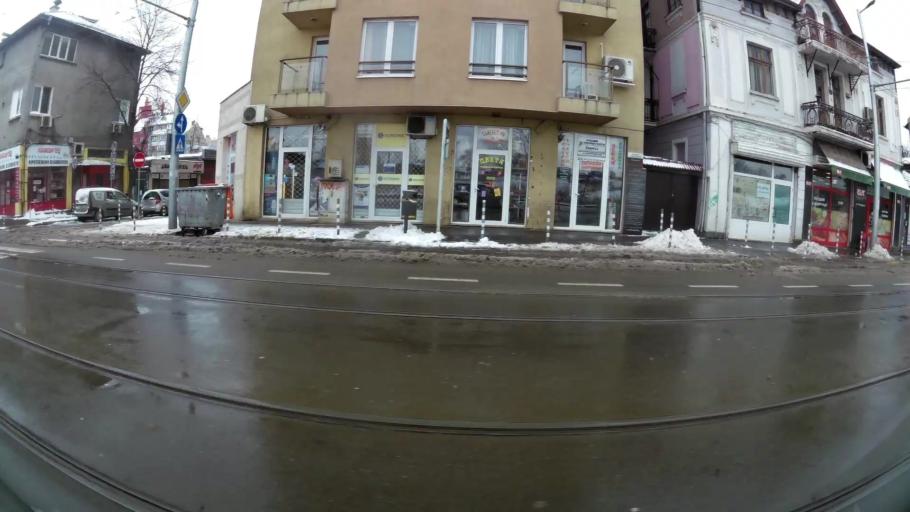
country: BG
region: Sofia-Capital
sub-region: Stolichna Obshtina
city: Sofia
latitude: 42.7079
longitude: 23.3296
